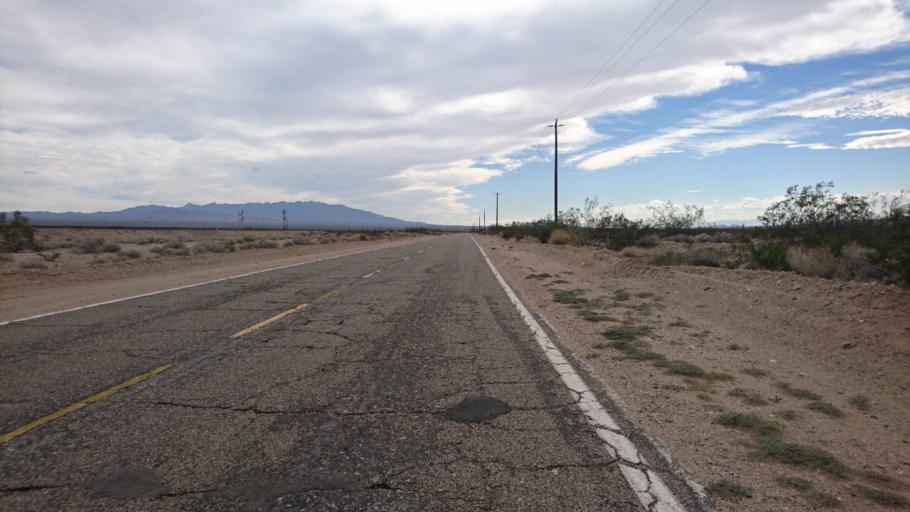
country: US
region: California
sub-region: San Bernardino County
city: Needles
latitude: 34.7681
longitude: -115.2136
